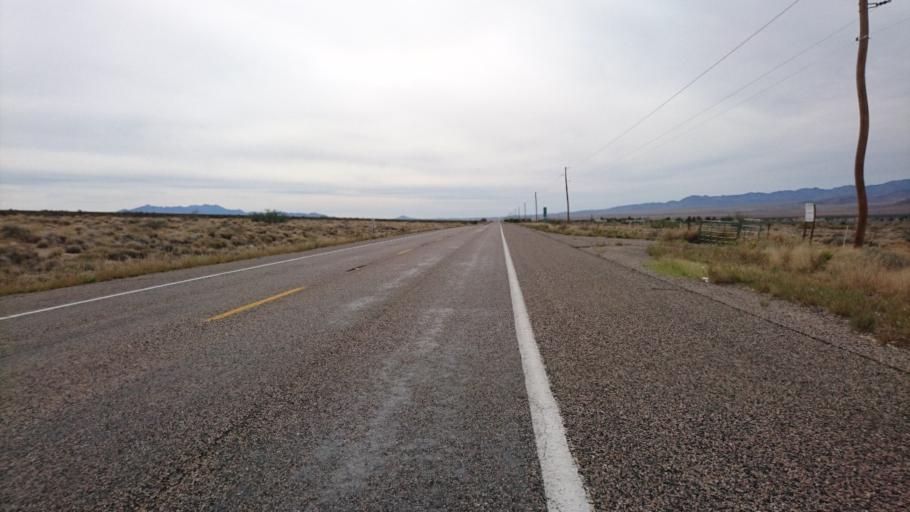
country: US
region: Arizona
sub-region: Mohave County
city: New Kingman-Butler
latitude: 35.4037
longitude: -113.8322
